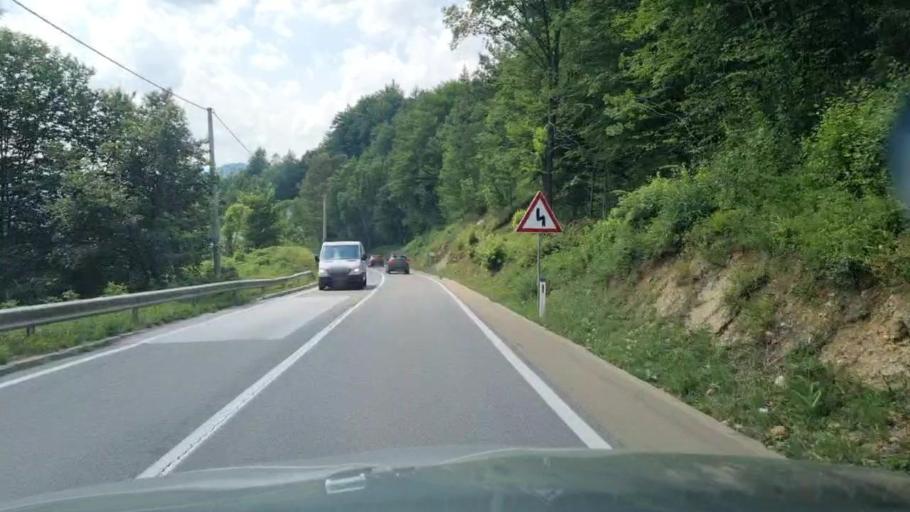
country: BA
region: Federation of Bosnia and Herzegovina
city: Kladanj
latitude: 44.2404
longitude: 18.7289
